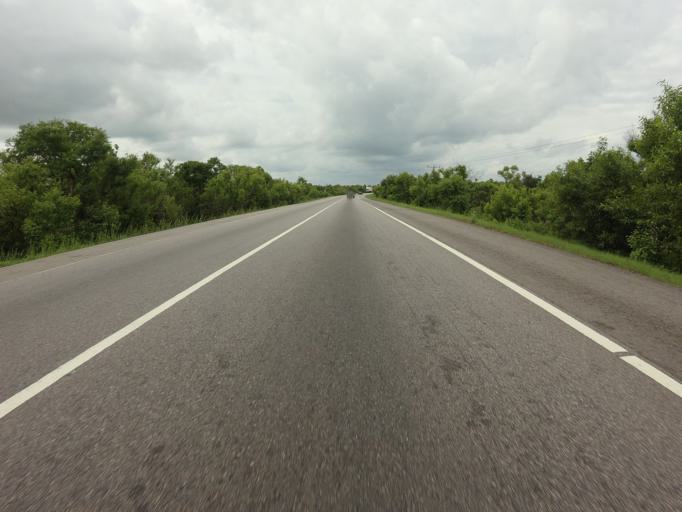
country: GH
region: Northern
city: Tamale
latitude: 8.8946
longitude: -1.4158
